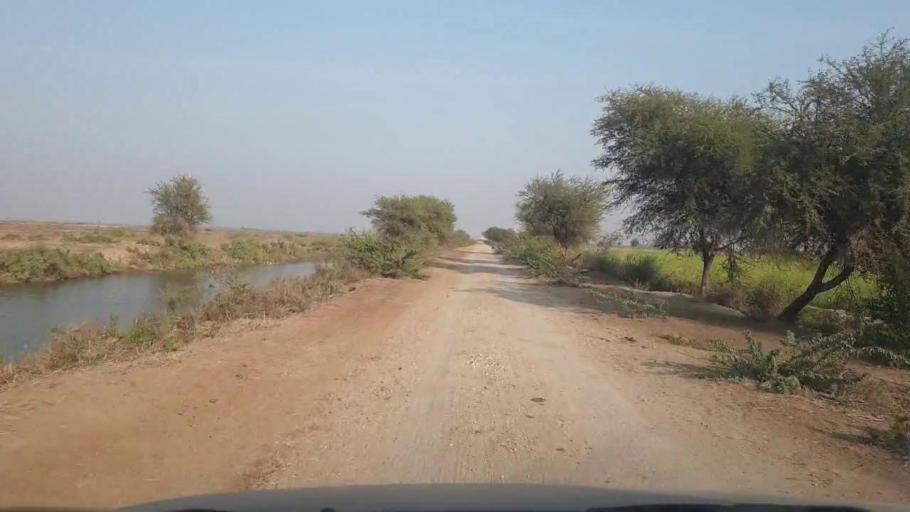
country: PK
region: Sindh
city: Mirwah Gorchani
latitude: 25.2950
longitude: 69.1699
